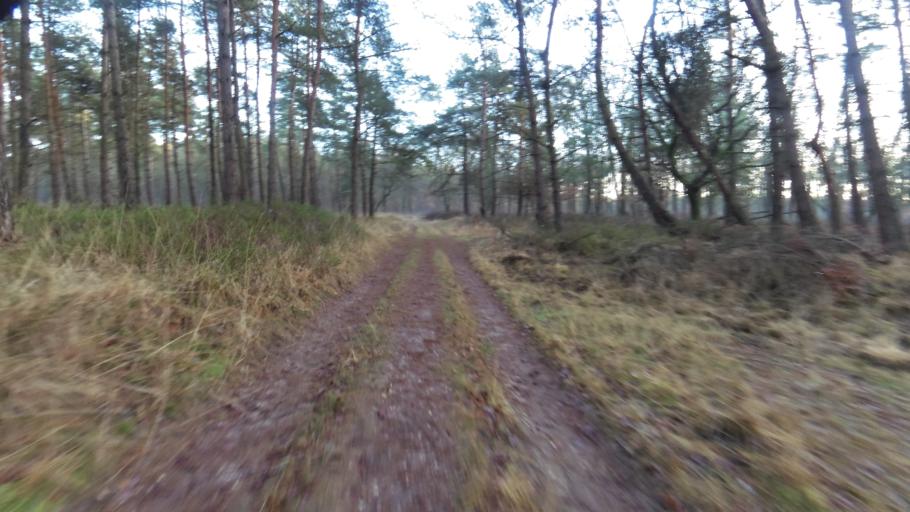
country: NL
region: Gelderland
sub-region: Gemeente Apeldoorn
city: Uddel
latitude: 52.2314
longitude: 5.8235
